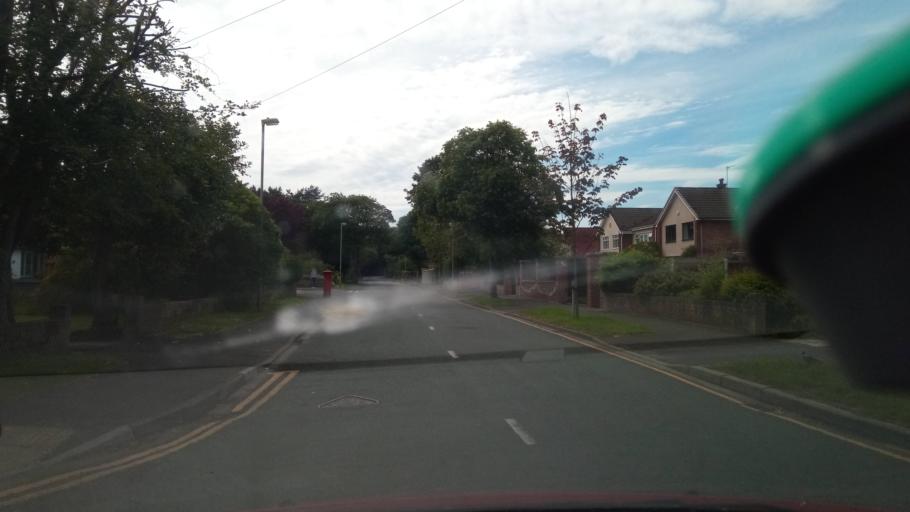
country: GB
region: England
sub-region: Sefton
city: Formby
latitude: 53.5511
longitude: -3.0827
